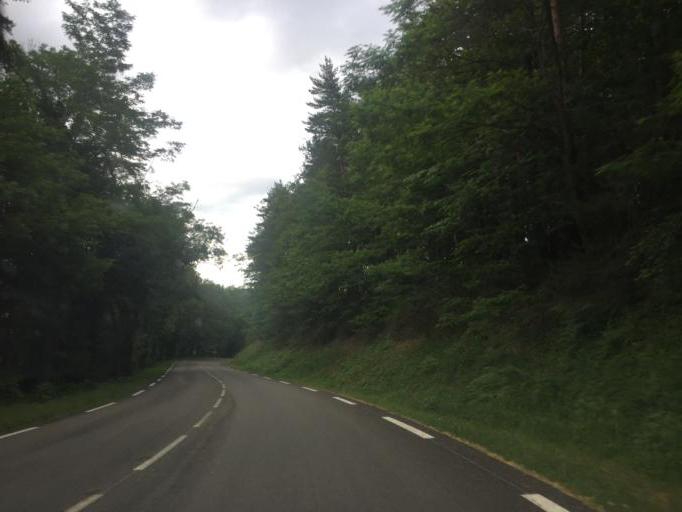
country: FR
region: Rhone-Alpes
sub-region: Departement de l'Ardeche
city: Privas
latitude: 44.7689
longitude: 4.5906
